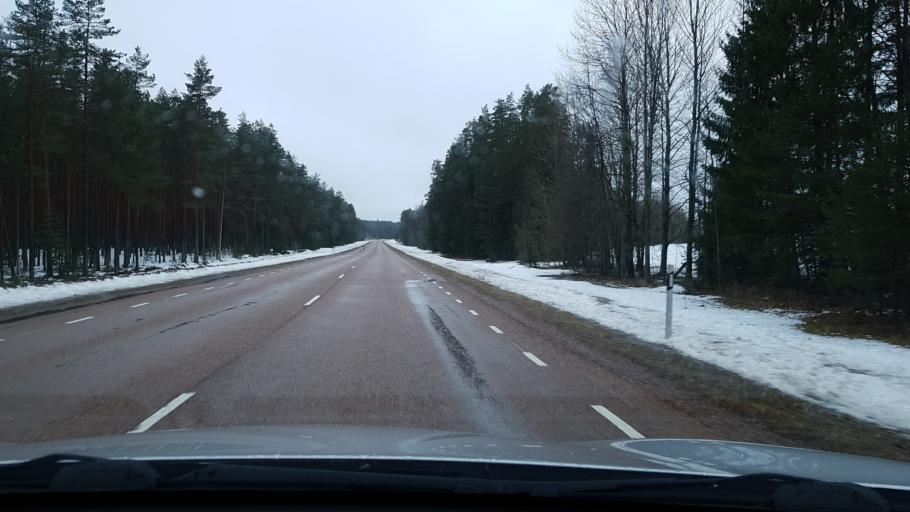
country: EE
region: Vorumaa
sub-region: Voru linn
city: Voru
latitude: 57.7679
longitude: 26.8555
